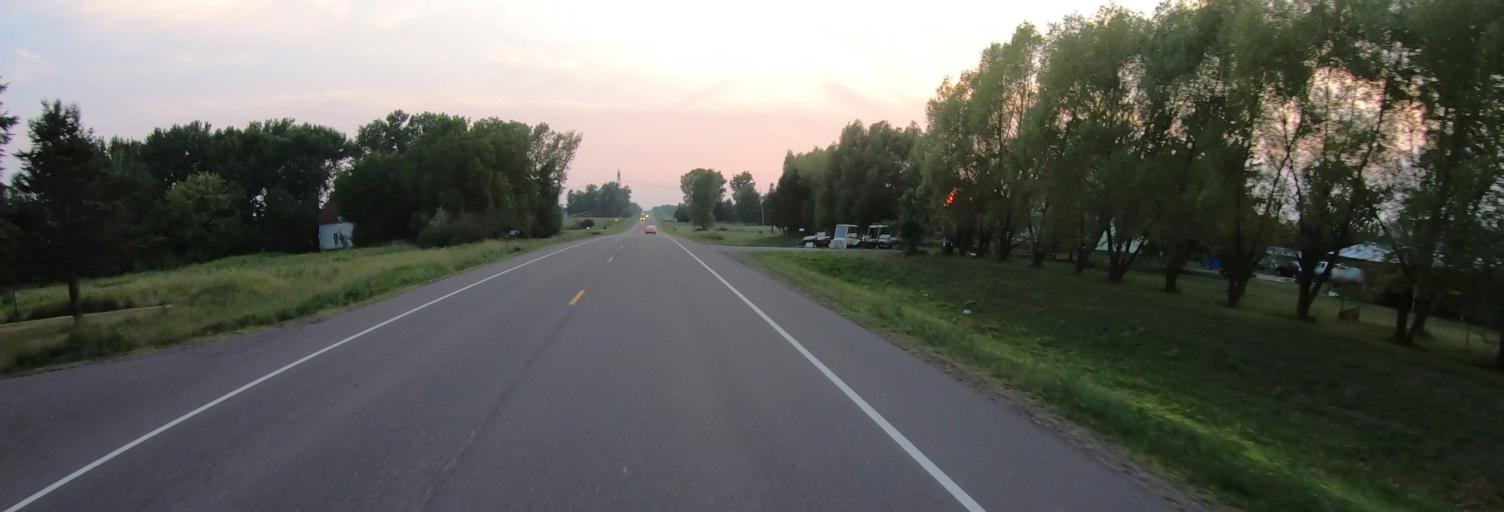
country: US
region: Minnesota
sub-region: Pine County
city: Rock Creek
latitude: 45.7734
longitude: -92.9009
